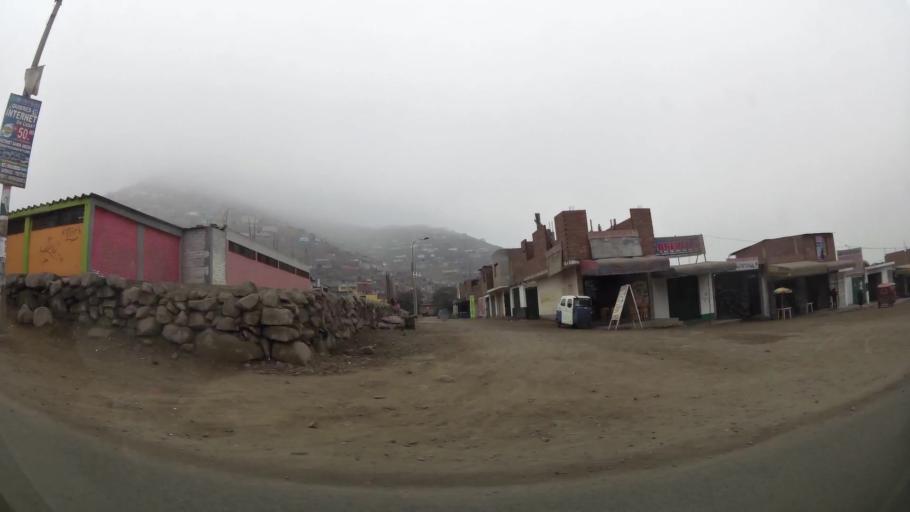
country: PE
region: Lima
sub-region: Lima
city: Urb. Santo Domingo
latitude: -11.8769
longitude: -77.0098
